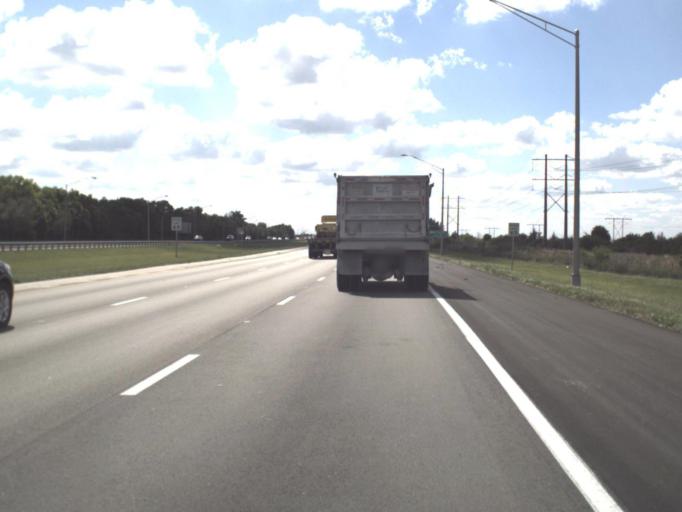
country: US
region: Florida
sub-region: Broward County
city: Tamarac
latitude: 26.1837
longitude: -80.3027
